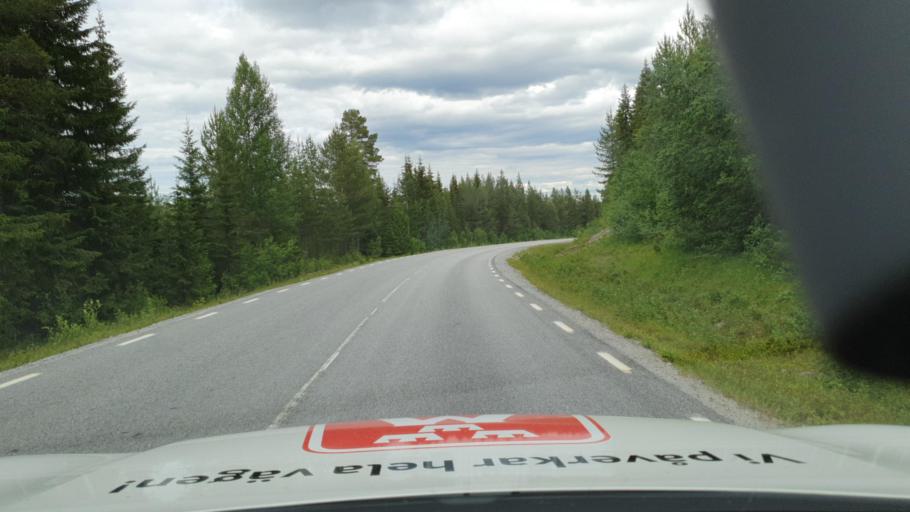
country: SE
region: Vaesterbotten
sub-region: Bjurholms Kommun
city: Bjurholm
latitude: 63.9008
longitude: 19.0759
